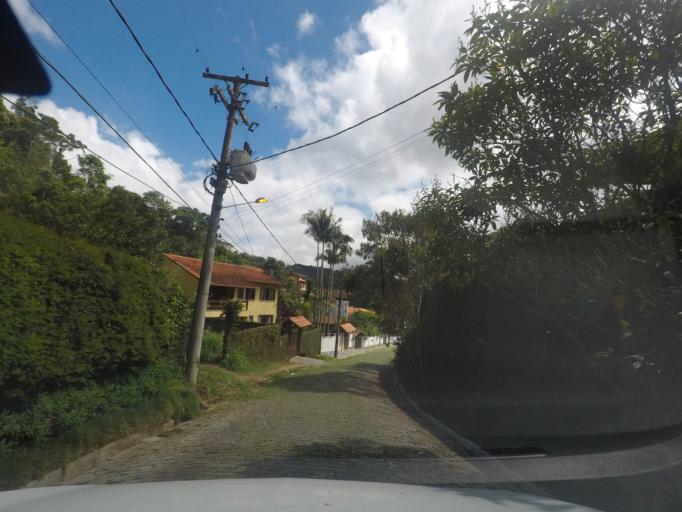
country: BR
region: Rio de Janeiro
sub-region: Teresopolis
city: Teresopolis
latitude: -22.3976
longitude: -42.9878
